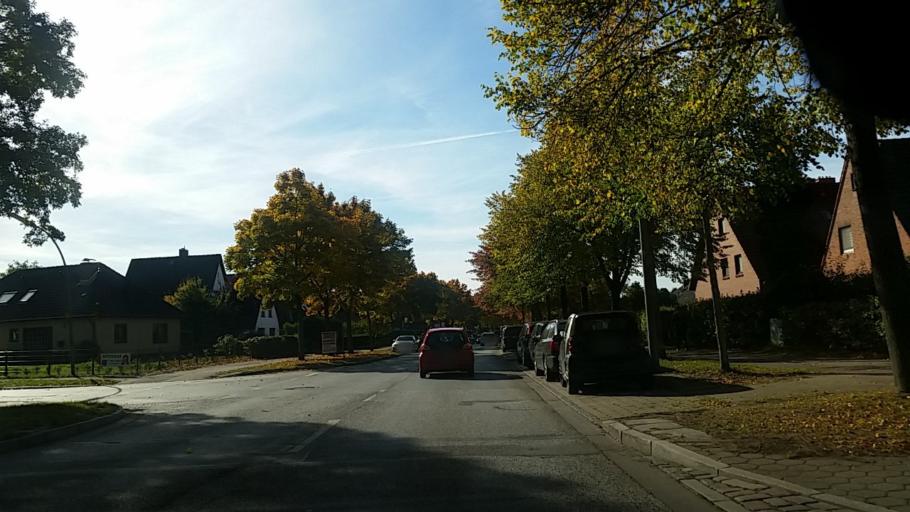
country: DE
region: Schleswig-Holstein
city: Oststeinbek
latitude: 53.5412
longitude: 10.1375
